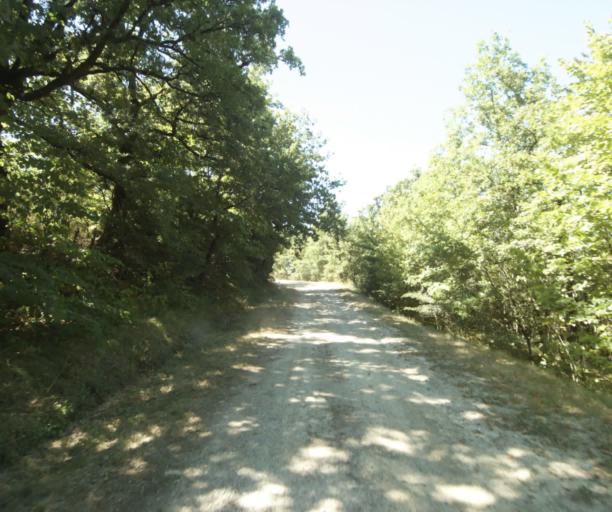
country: FR
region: Midi-Pyrenees
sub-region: Departement de la Haute-Garonne
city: Saint-Felix-Lauragais
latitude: 43.4835
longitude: 1.9222
